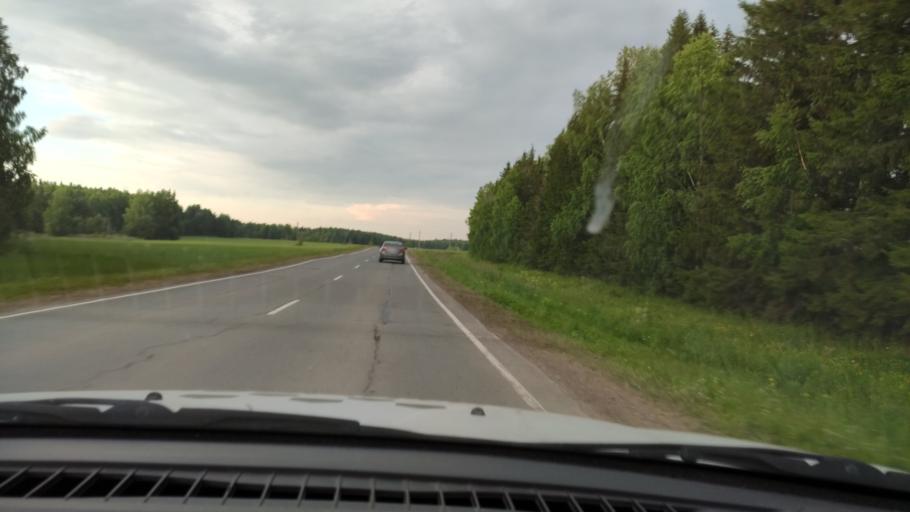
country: RU
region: Perm
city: Kukushtan
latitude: 57.4740
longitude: 56.5694
